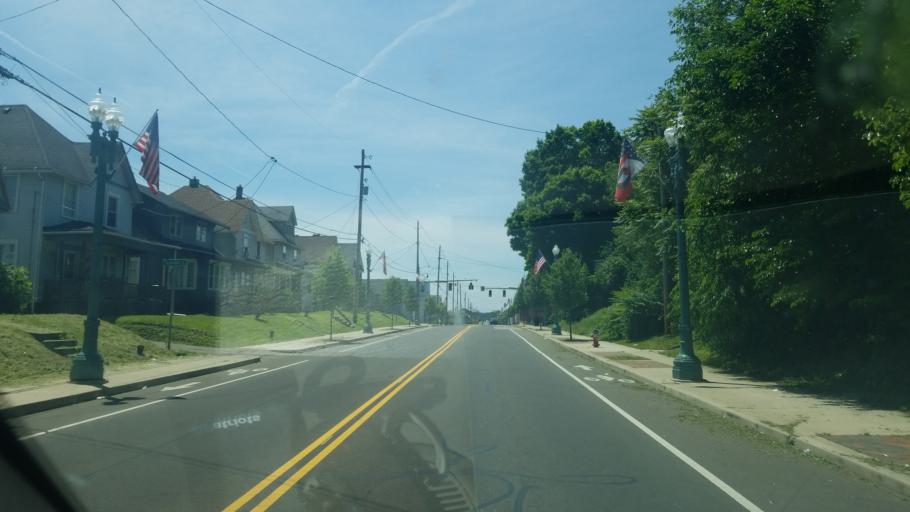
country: US
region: Ohio
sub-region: Stark County
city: Canton
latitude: 40.8089
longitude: -81.3613
